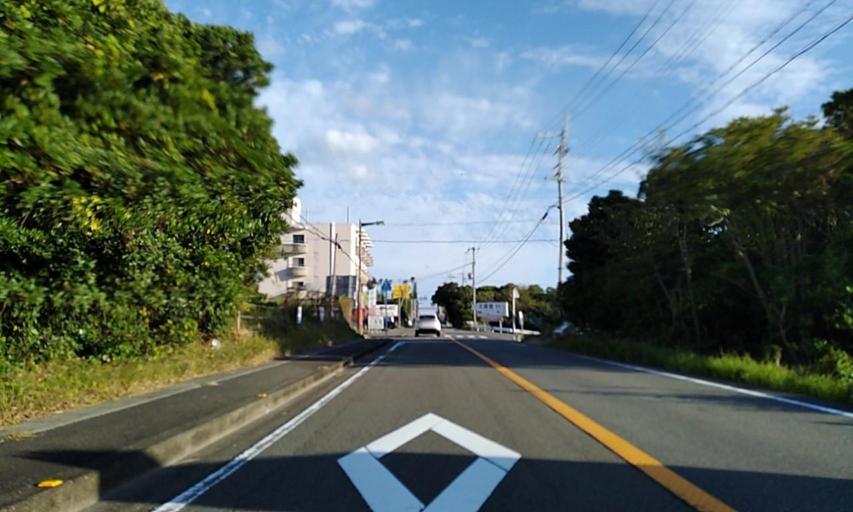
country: JP
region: Wakayama
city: Tanabe
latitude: 33.6678
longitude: 135.3349
